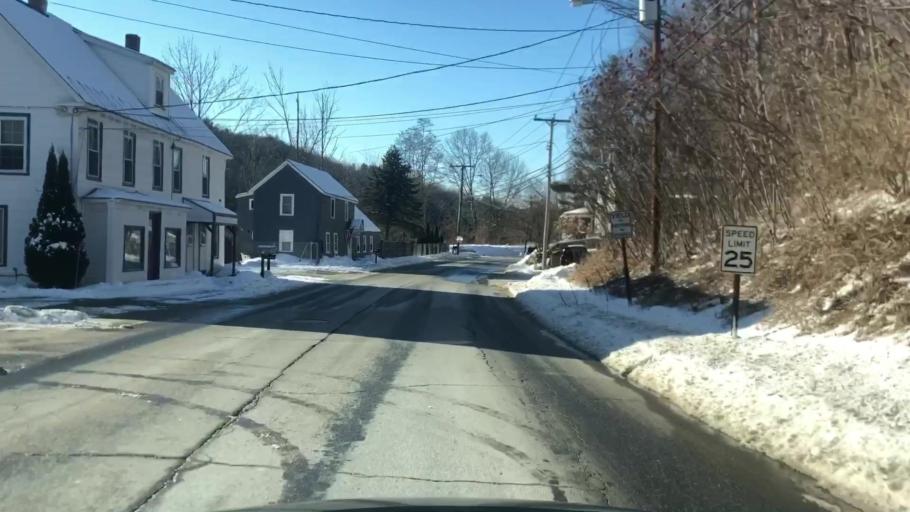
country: US
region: New Hampshire
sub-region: Hillsborough County
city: Wilton
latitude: 42.8396
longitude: -71.7281
